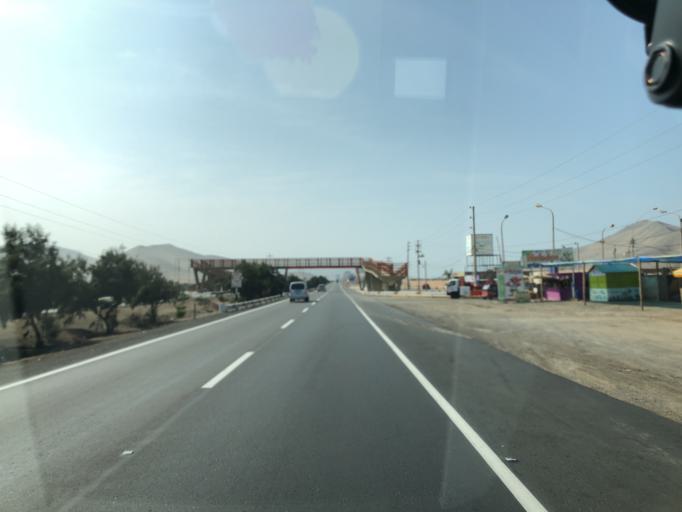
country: PE
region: Lima
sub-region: Provincia de Canete
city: Chilca
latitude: -12.5389
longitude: -76.7186
